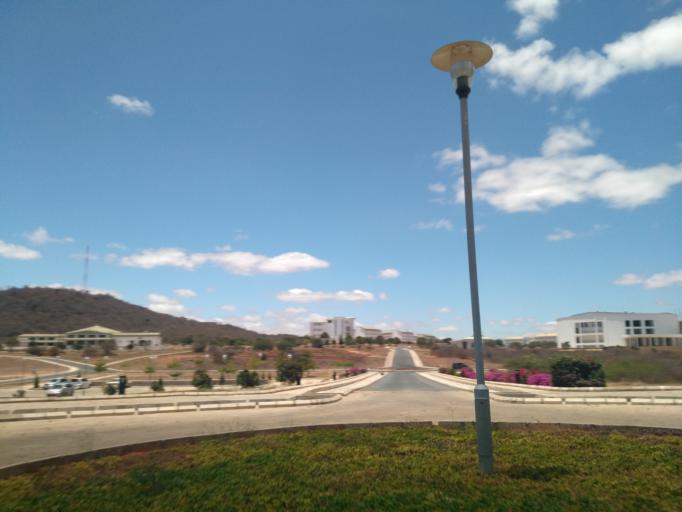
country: TZ
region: Dodoma
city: Kisasa
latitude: -6.2161
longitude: 35.8088
